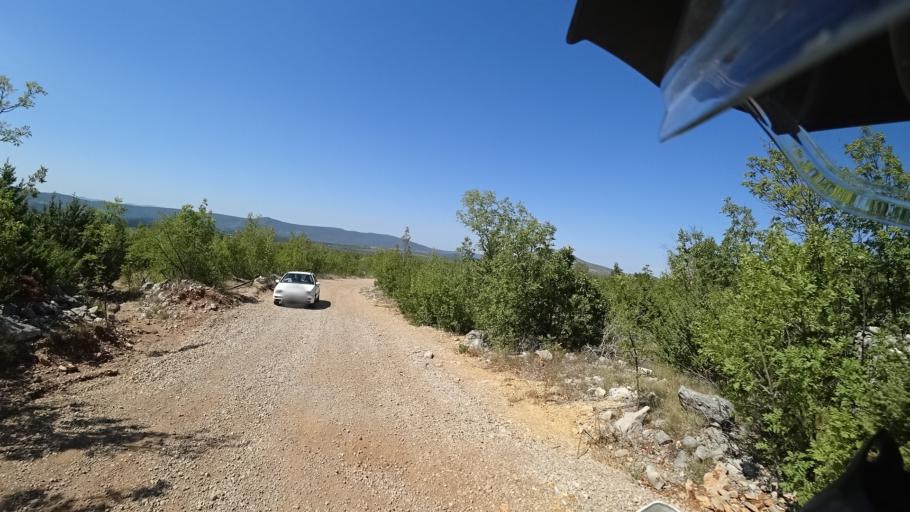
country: HR
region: Splitsko-Dalmatinska
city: Hrvace
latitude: 43.7542
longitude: 16.4503
